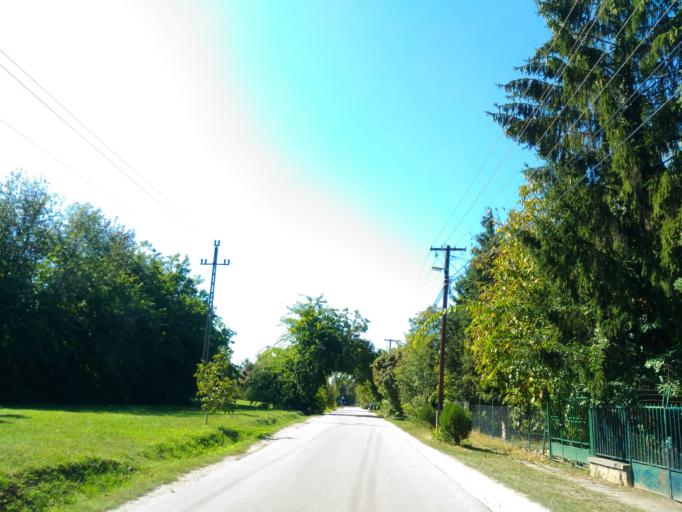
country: HU
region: Fejer
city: Gardony
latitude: 47.1941
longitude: 18.6119
